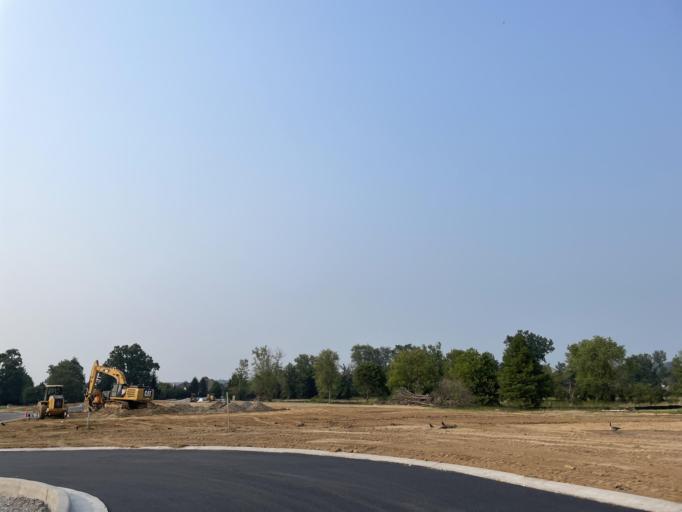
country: US
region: Kentucky
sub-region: Jefferson County
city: Prospect
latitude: 38.3569
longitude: -85.6261
